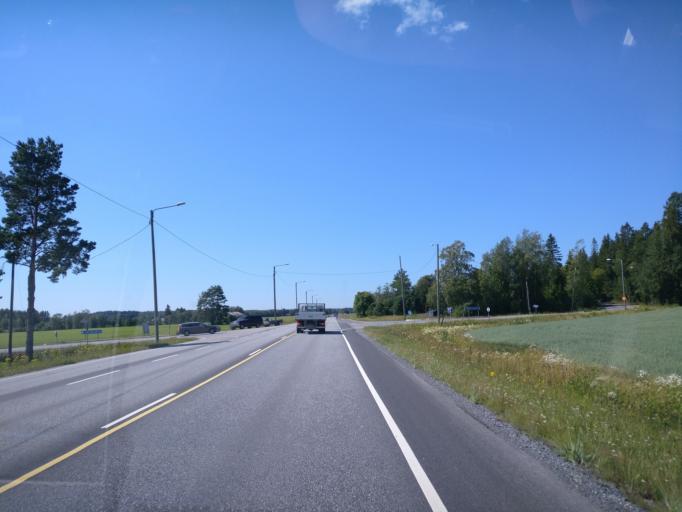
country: FI
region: Satakunta
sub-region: Pori
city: Nakkila
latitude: 61.4596
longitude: 22.0128
